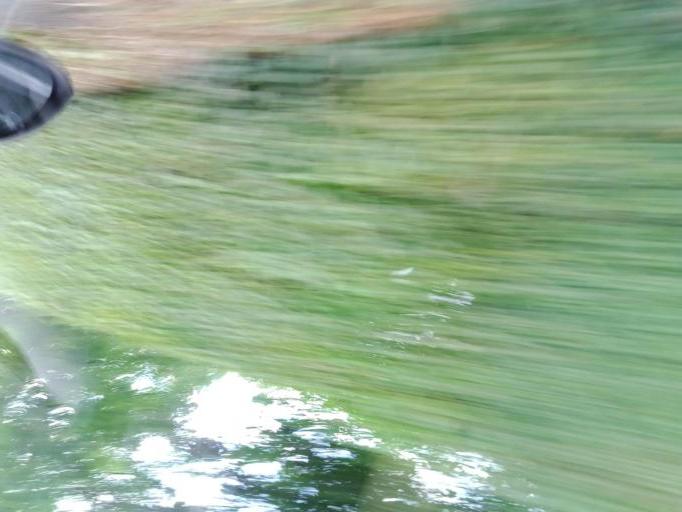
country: IE
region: Leinster
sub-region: Laois
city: Portlaoise
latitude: 53.0533
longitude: -7.3165
